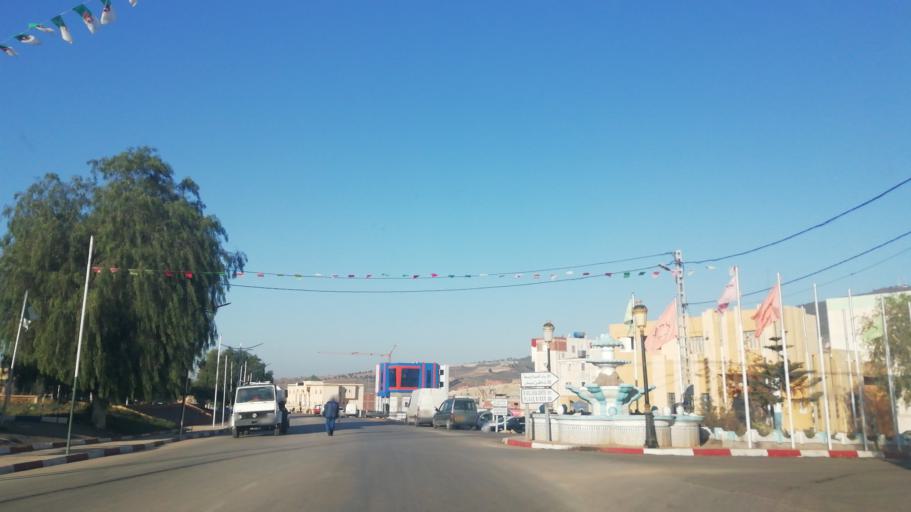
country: MA
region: Oriental
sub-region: Berkane-Taourirt
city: Ahfir
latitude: 34.9614
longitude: -2.0309
